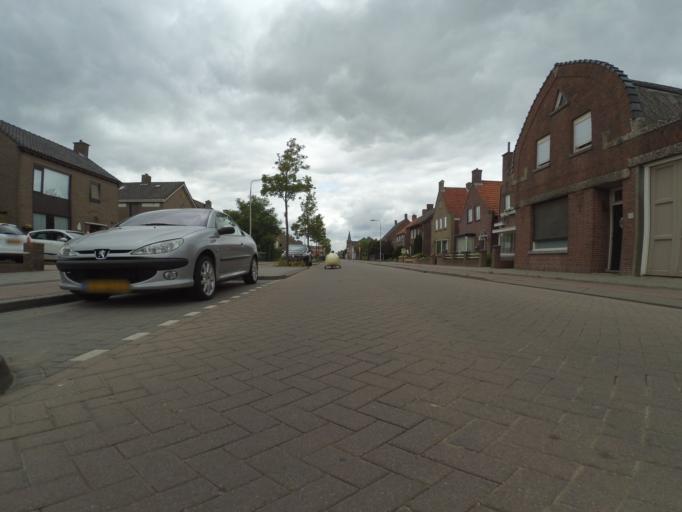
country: NL
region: North Brabant
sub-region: Gemeente Steenbergen
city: Kruisland
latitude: 51.5658
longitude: 4.4079
